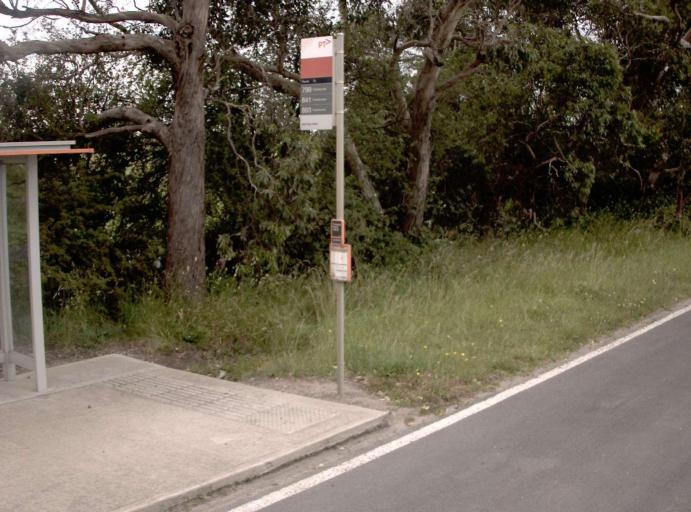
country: AU
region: Victoria
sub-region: Casey
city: Cranbourne
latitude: -38.0934
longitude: 145.2815
